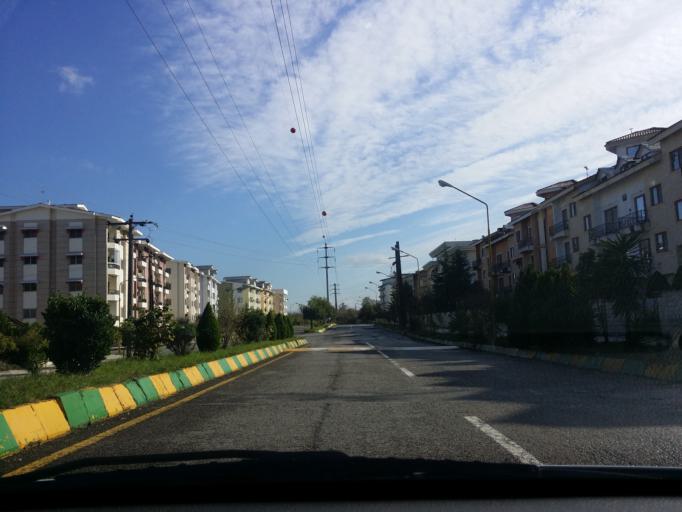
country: IR
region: Mazandaran
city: Chalus
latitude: 36.6747
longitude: 51.3106
